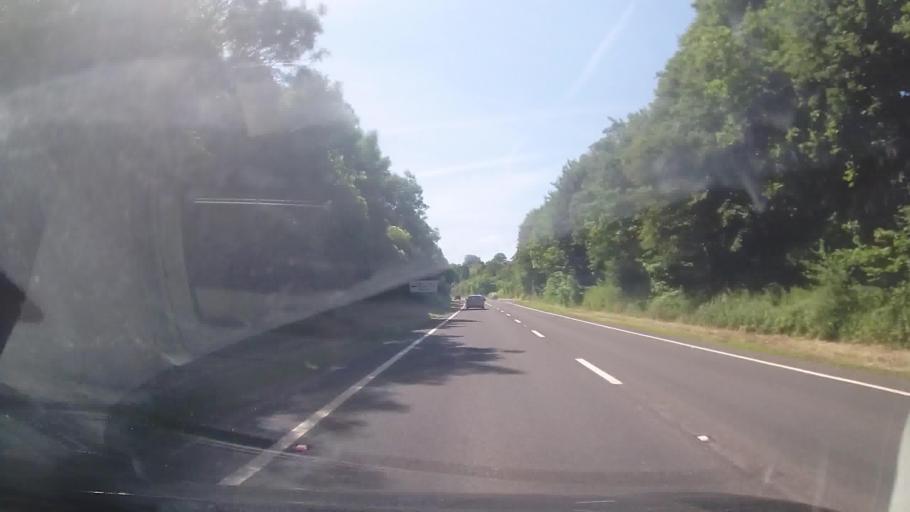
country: GB
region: England
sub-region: Herefordshire
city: Hope under Dinmore
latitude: 52.1956
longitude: -2.7183
